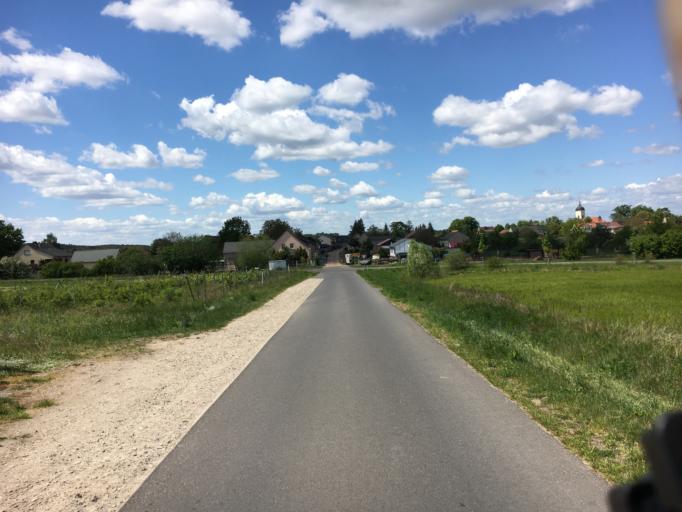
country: DE
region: Brandenburg
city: Trebbin
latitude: 52.2110
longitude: 13.2844
